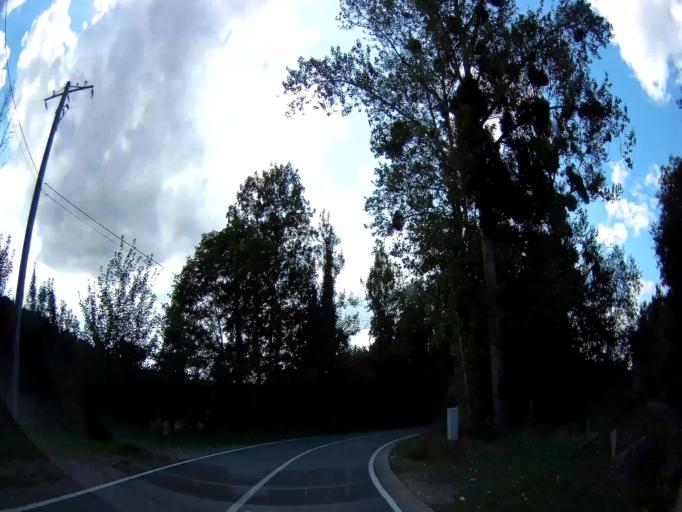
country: BE
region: Wallonia
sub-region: Province de Namur
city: Anhee
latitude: 50.3169
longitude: 4.8647
